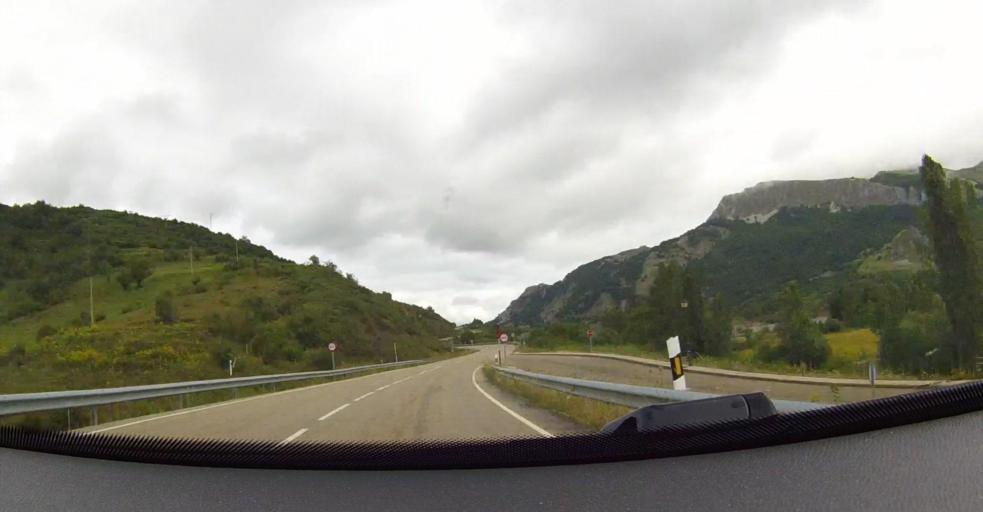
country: ES
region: Castille and Leon
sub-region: Provincia de Leon
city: Buron
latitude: 43.0247
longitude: -5.0468
